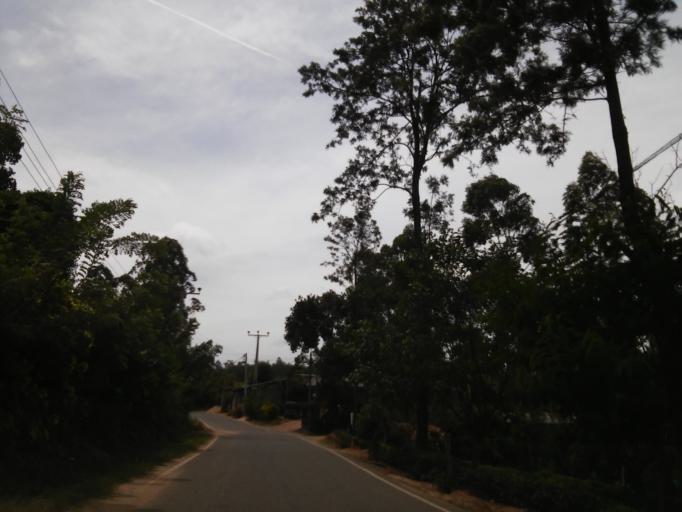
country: LK
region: Uva
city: Haputale
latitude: 6.8494
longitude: 81.0251
